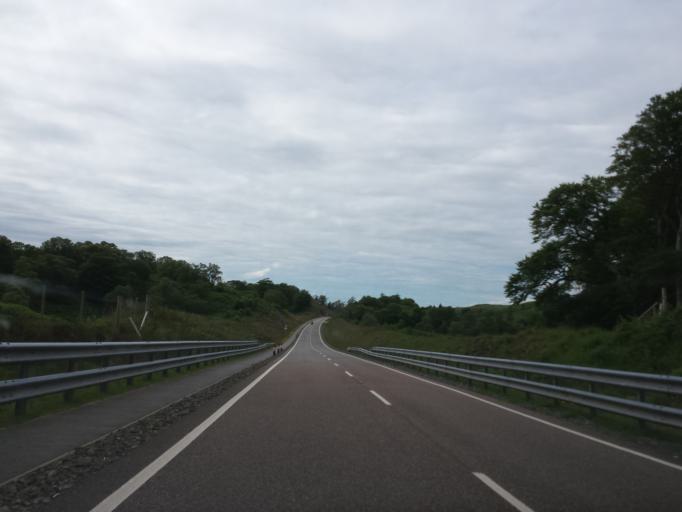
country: GB
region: Scotland
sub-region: Argyll and Bute
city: Isle Of Mull
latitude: 56.9027
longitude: -5.8096
